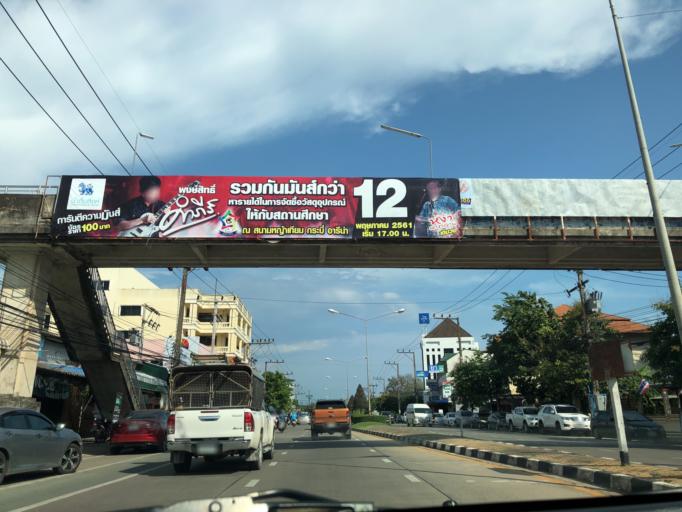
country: TH
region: Krabi
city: Krabi
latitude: 8.0763
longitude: 98.9158
